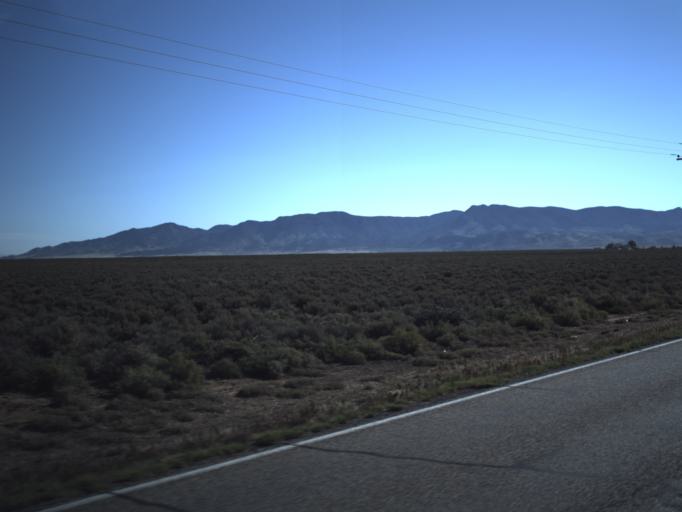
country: US
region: Utah
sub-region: Washington County
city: Enterprise
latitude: 37.6967
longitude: -113.6207
